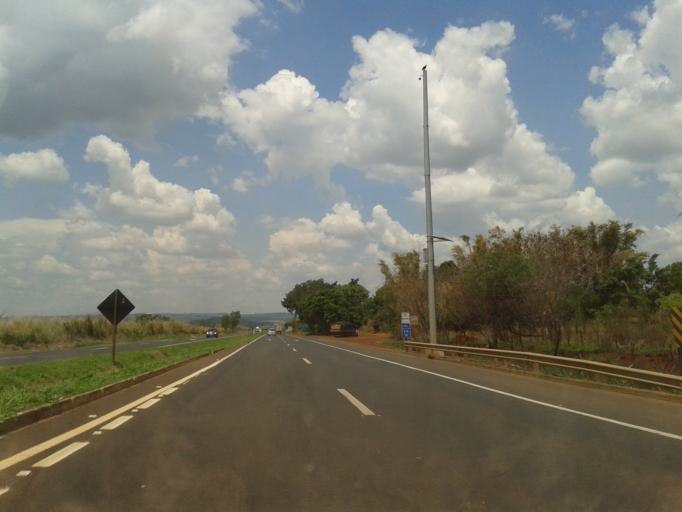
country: BR
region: Minas Gerais
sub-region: Araguari
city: Araguari
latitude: -18.7371
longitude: -48.2277
